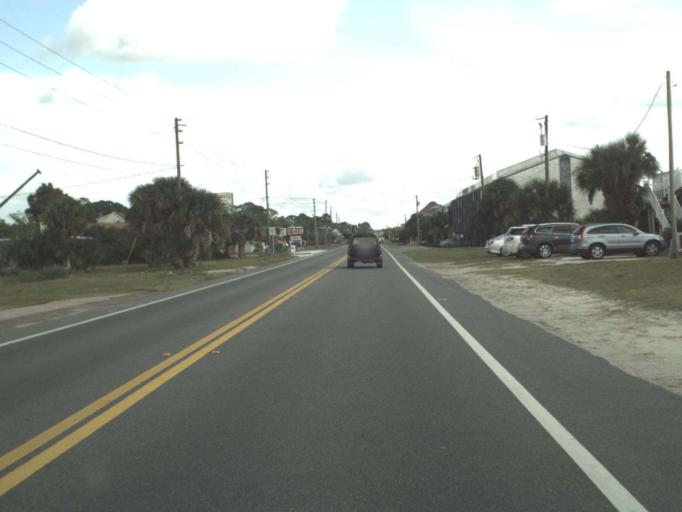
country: US
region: Florida
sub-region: Bay County
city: Mexico Beach
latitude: 29.9091
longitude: -85.3723
